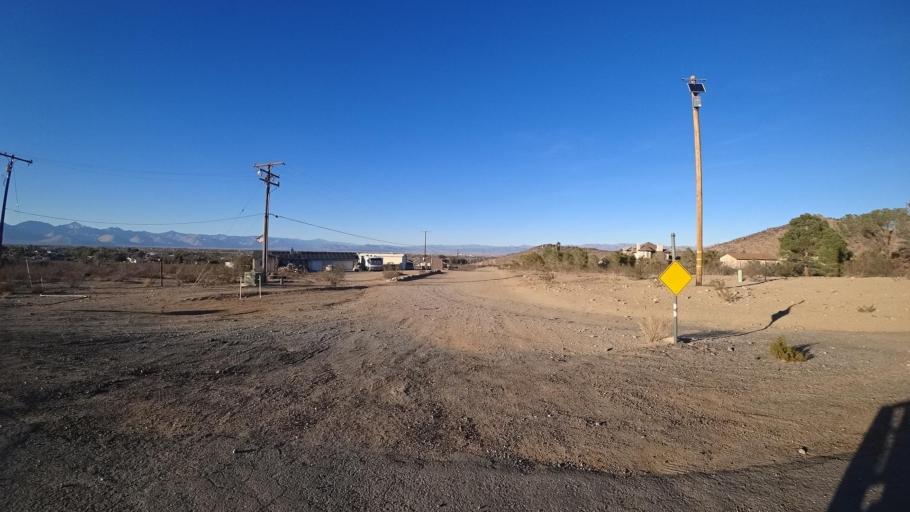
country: US
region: California
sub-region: Kern County
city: Ridgecrest
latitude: 35.5786
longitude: -117.6522
